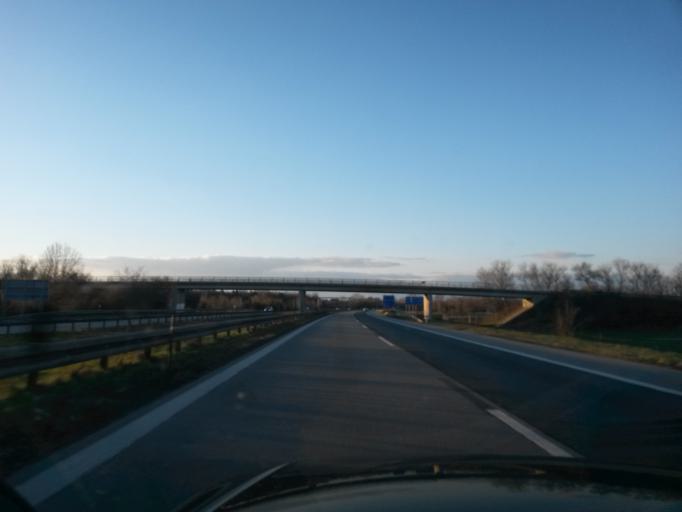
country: DE
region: Bavaria
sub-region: Upper Bavaria
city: Oberschleissheim
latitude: 48.2440
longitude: 11.5342
